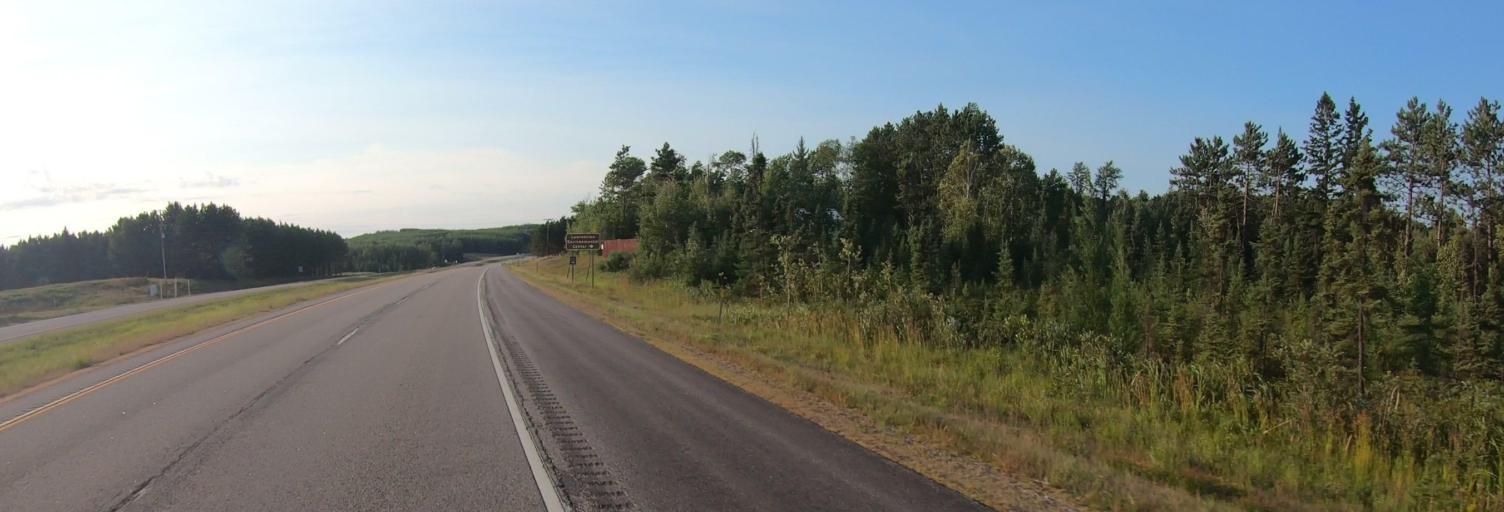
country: US
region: Minnesota
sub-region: Saint Louis County
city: Mountain Iron
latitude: 47.6749
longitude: -92.6339
